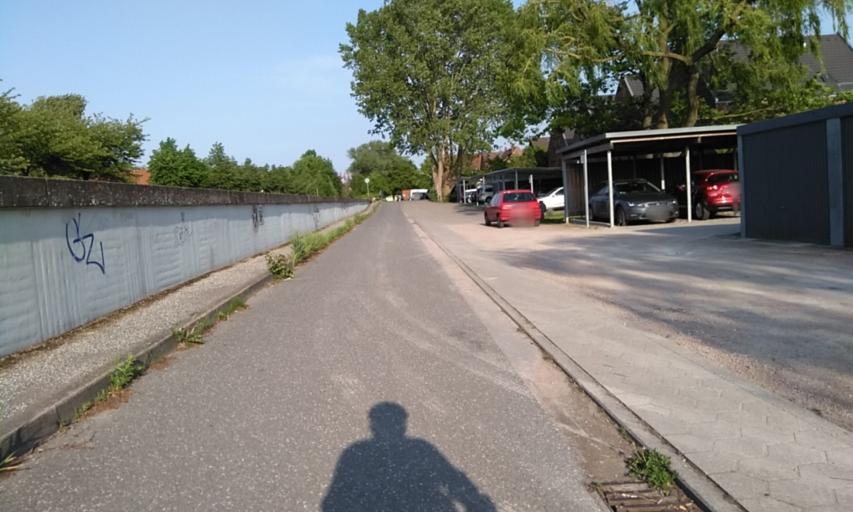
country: DE
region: Hamburg
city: Altona
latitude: 53.5346
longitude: 9.8708
